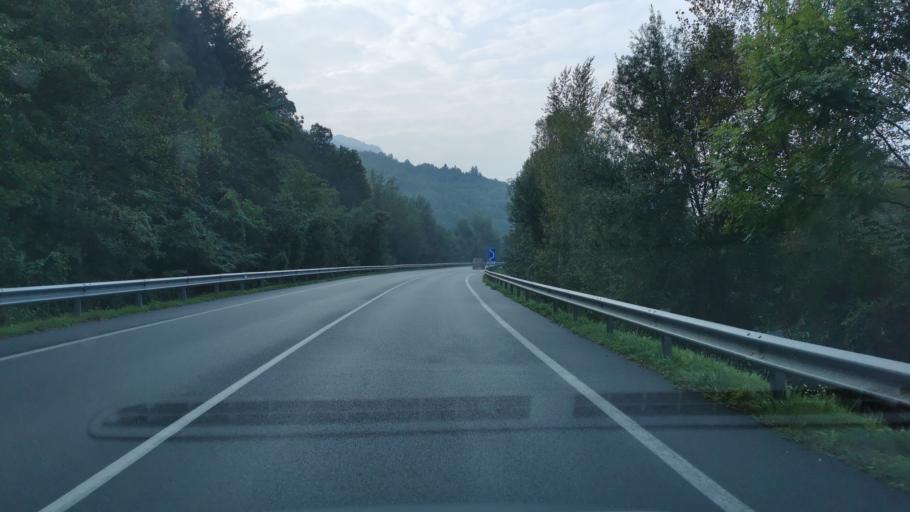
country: IT
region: Piedmont
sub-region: Provincia di Cuneo
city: Robilante
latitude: 44.3010
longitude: 7.5162
